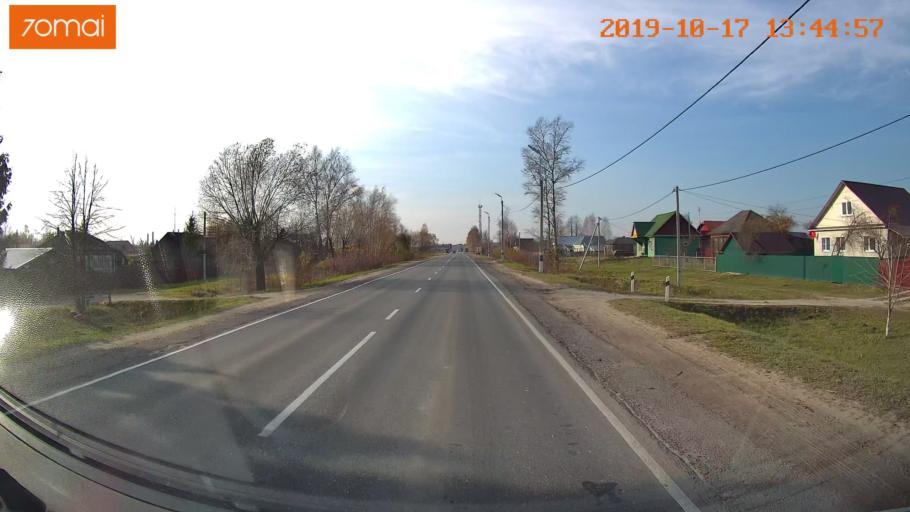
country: RU
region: Rjazan
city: Tuma
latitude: 55.1467
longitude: 40.5214
